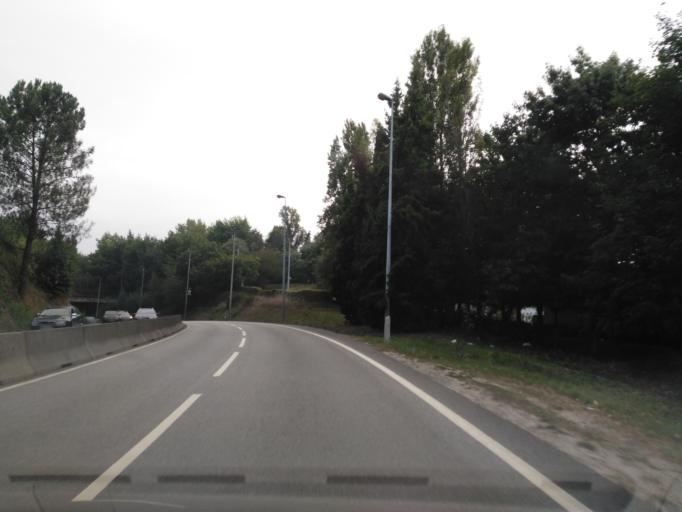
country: PT
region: Braga
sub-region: Guimaraes
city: Guimaraes
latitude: 41.4453
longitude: -8.3089
